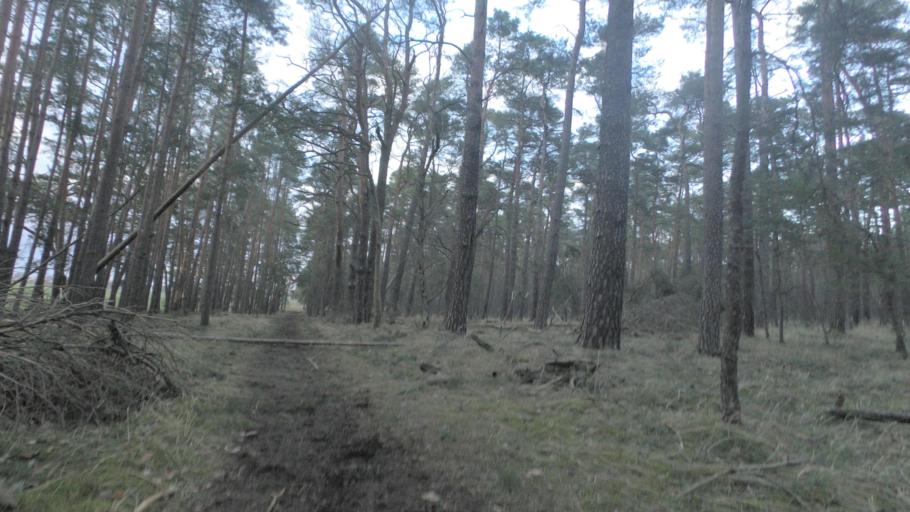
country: DE
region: Brandenburg
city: Rangsdorf
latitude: 52.2634
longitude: 13.3545
